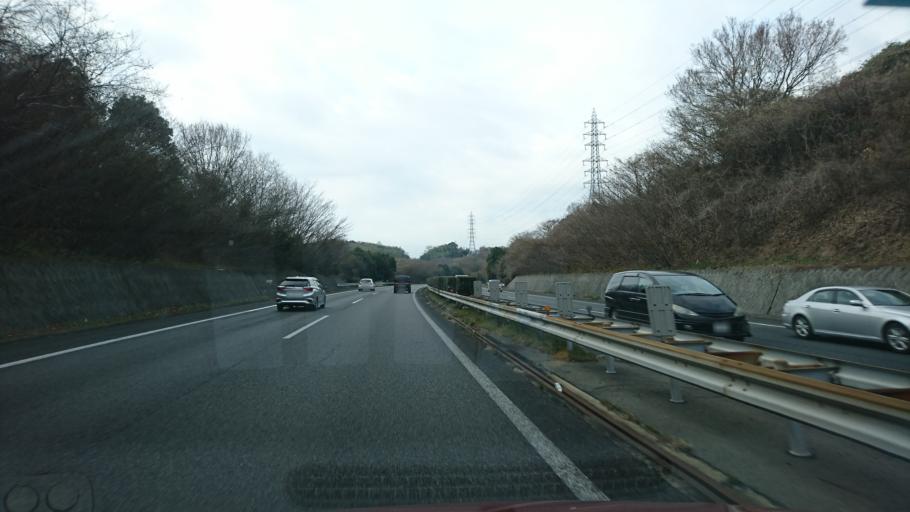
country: JP
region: Okayama
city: Kurashiki
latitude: 34.6052
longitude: 133.7256
